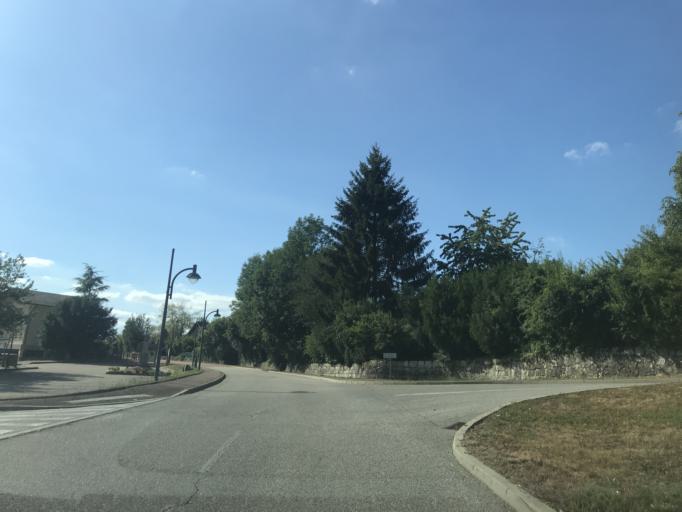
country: FR
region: Rhone-Alpes
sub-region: Departement de la Savoie
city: Yenne
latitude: 45.7188
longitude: 5.8108
